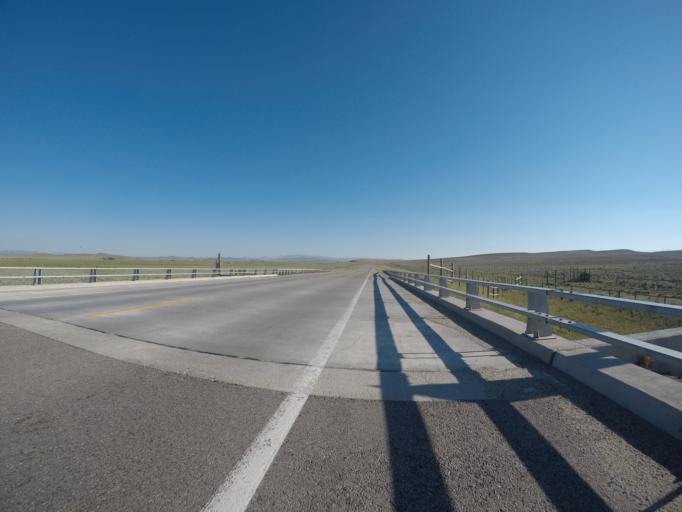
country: US
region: Wyoming
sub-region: Sublette County
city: Pinedale
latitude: 42.9253
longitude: -110.0808
